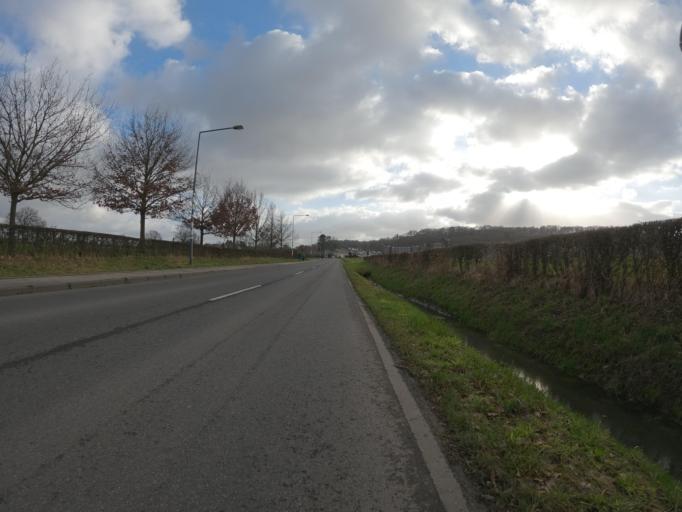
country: DE
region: North Rhine-Westphalia
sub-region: Regierungsbezirk Koln
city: Aachen
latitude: 50.7960
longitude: 6.0842
